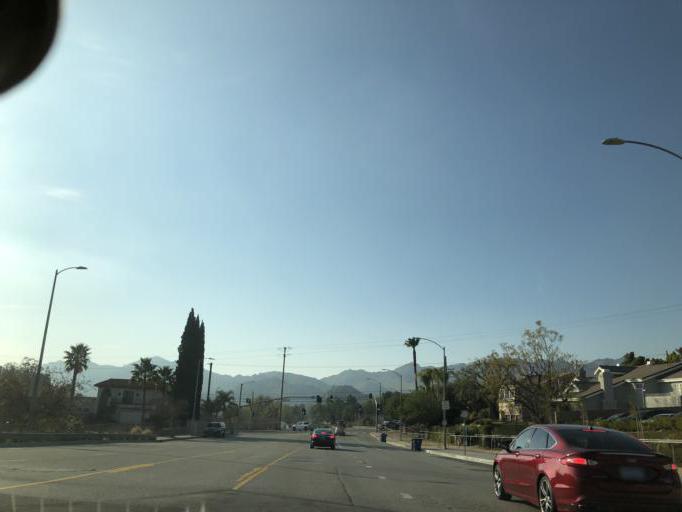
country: US
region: California
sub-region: Los Angeles County
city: Chatsworth
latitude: 34.2700
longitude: -118.5872
